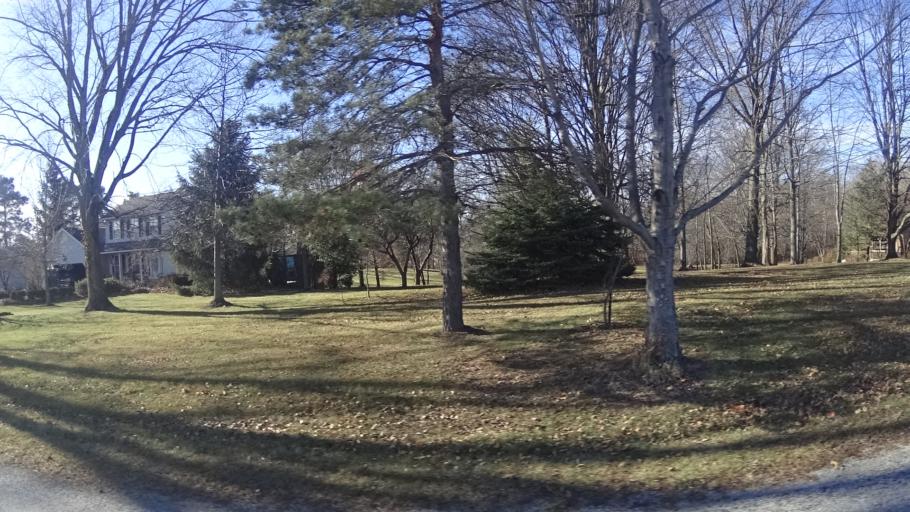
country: US
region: Ohio
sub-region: Huron County
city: Wakeman
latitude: 41.3222
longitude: -82.3439
